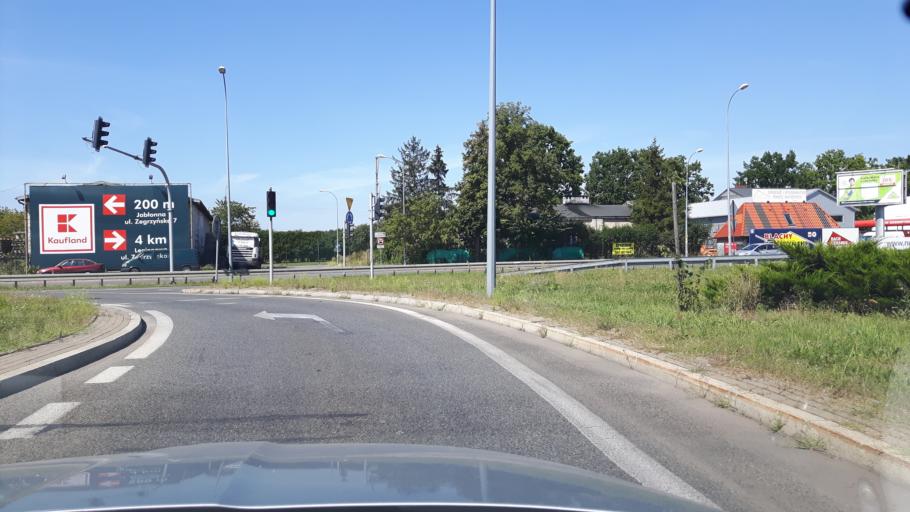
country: PL
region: Masovian Voivodeship
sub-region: Powiat legionowski
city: Jablonna
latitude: 52.3811
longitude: 20.9213
